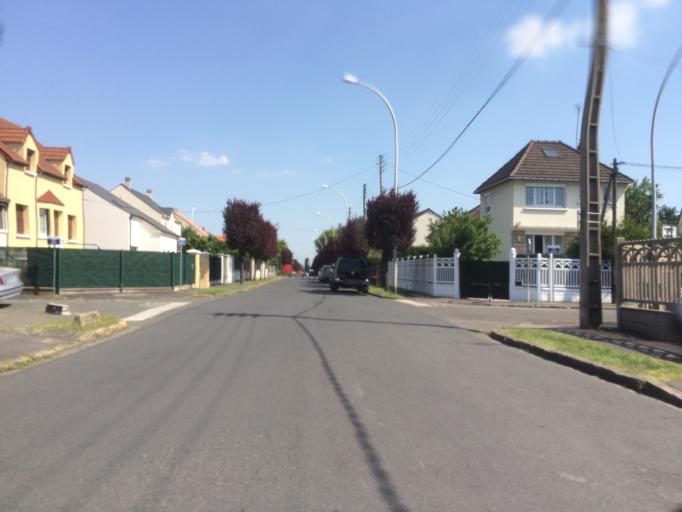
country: FR
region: Ile-de-France
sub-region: Departement de l'Essonne
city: Morangis
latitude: 48.6936
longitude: 2.3443
